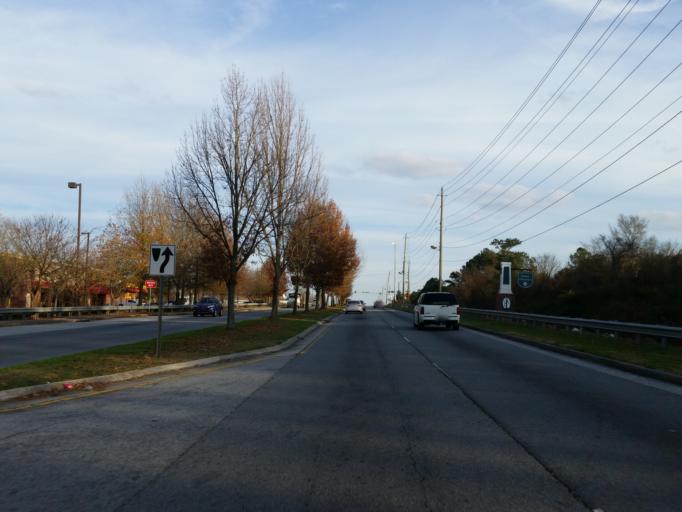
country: US
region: Georgia
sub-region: Cobb County
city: Powder Springs
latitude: 33.8639
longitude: -84.6789
